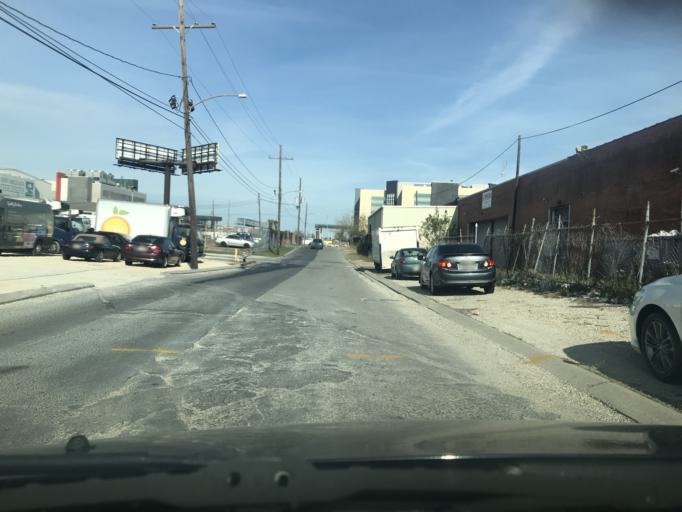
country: US
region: Louisiana
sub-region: Orleans Parish
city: New Orleans
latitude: 29.9577
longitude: -90.0977
